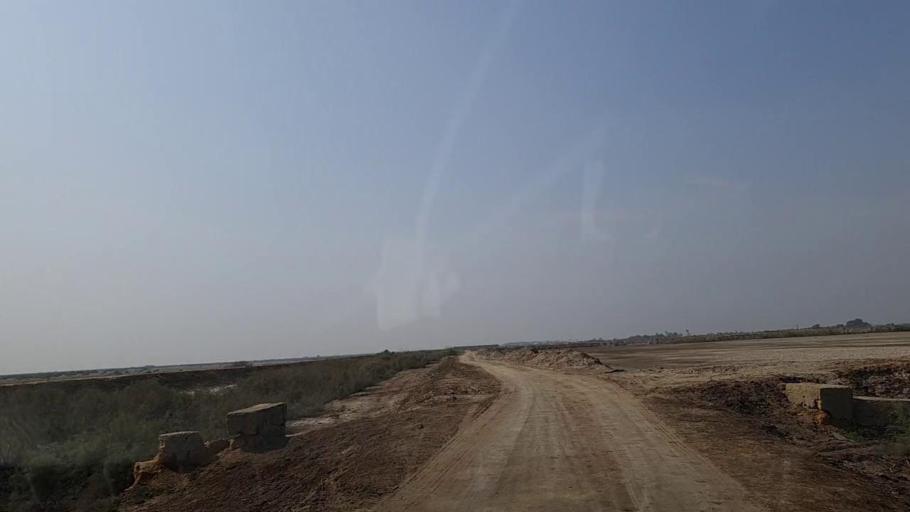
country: PK
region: Sindh
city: Gharo
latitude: 24.6737
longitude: 67.7173
